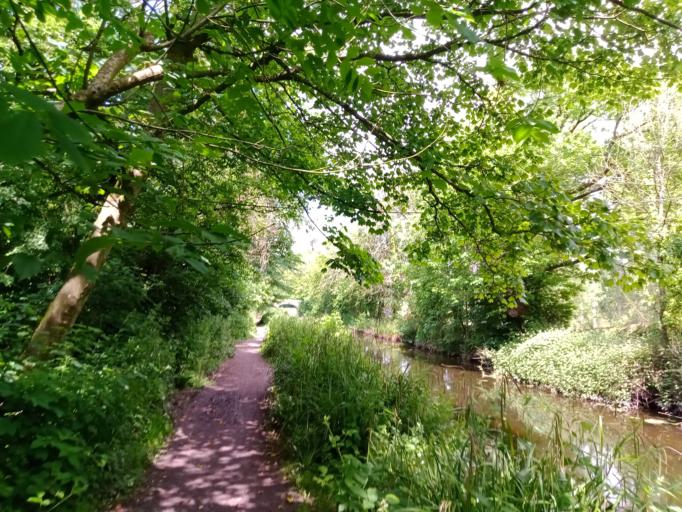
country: IE
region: Leinster
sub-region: County Carlow
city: Carlow
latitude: 52.7801
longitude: -6.9648
